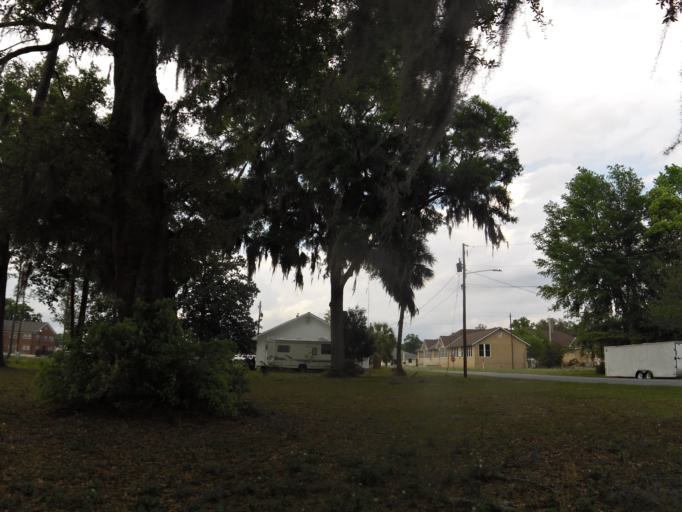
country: US
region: Georgia
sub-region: Charlton County
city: Folkston
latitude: 30.8300
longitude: -82.0040
